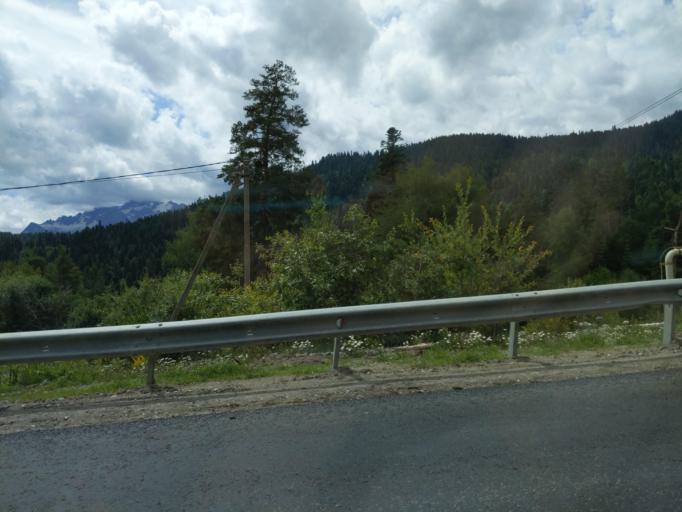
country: RU
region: Karachayevo-Cherkesiya
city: Nizhniy Arkhyz
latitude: 43.5371
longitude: 41.2084
